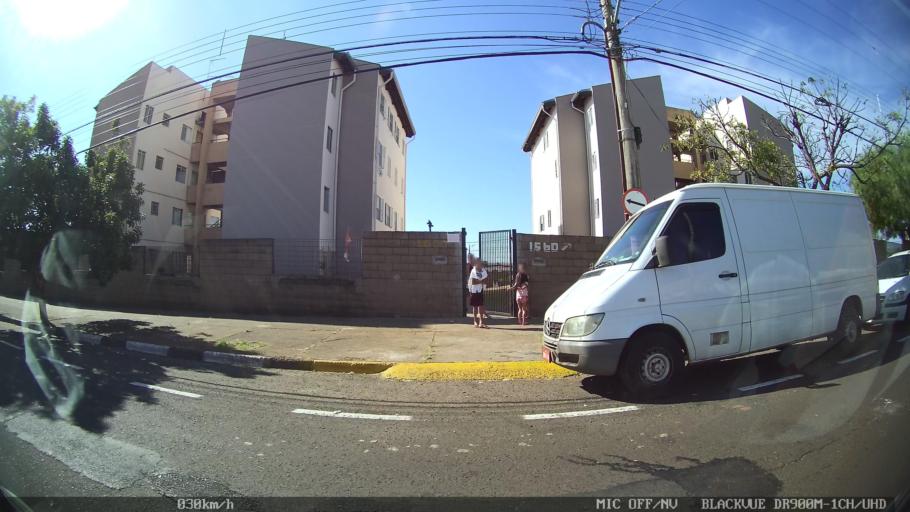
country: BR
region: Sao Paulo
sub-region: Franca
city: Franca
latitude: -20.4965
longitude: -47.4213
